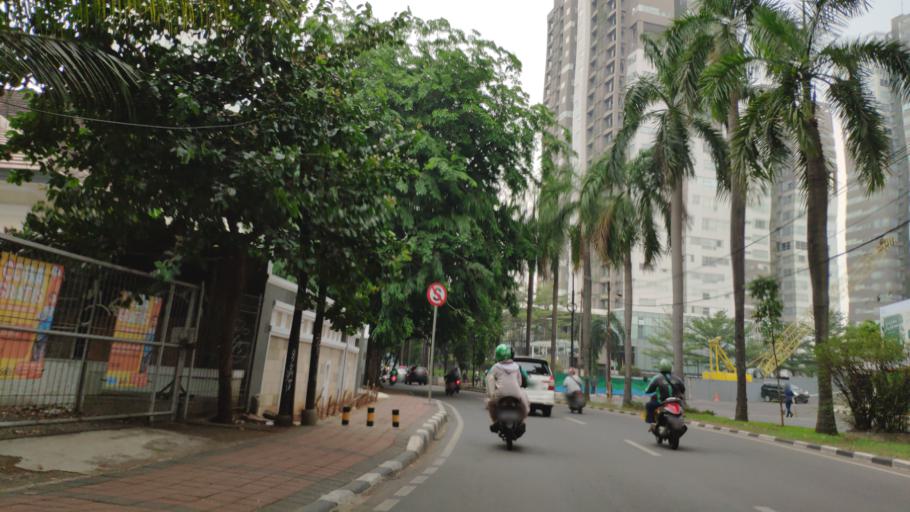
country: ID
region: Jakarta Raya
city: Jakarta
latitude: -6.2457
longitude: 106.7873
